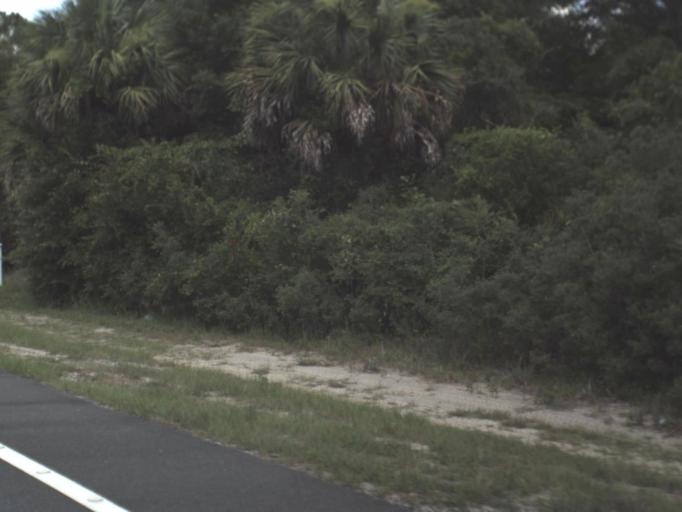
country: US
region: Florida
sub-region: Levy County
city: Chiefland
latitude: 29.2193
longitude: -82.9636
